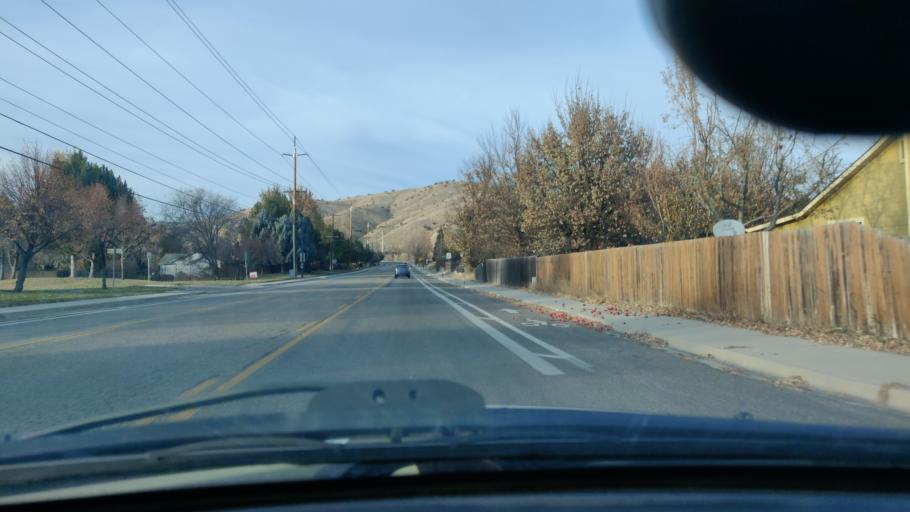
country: US
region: Idaho
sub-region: Ada County
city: Garden City
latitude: 43.6802
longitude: -116.2792
